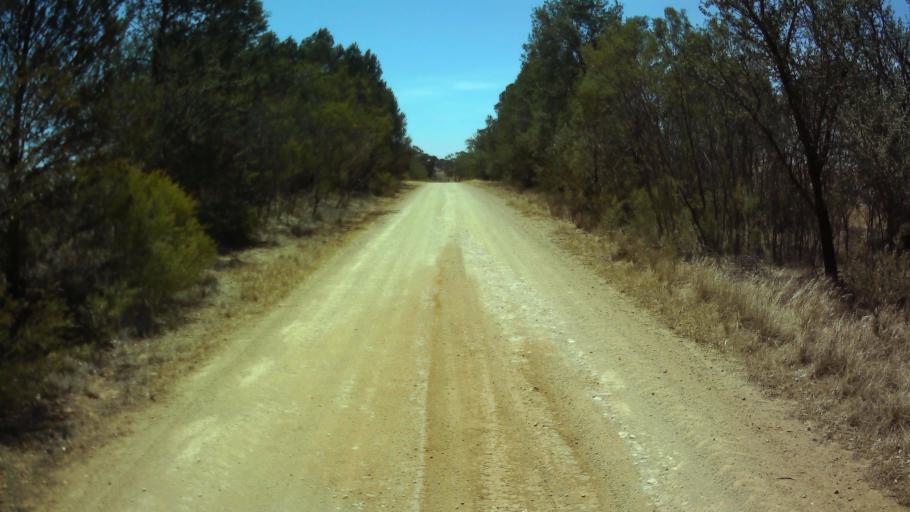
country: AU
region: New South Wales
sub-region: Weddin
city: Grenfell
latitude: -33.9265
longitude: 148.1783
